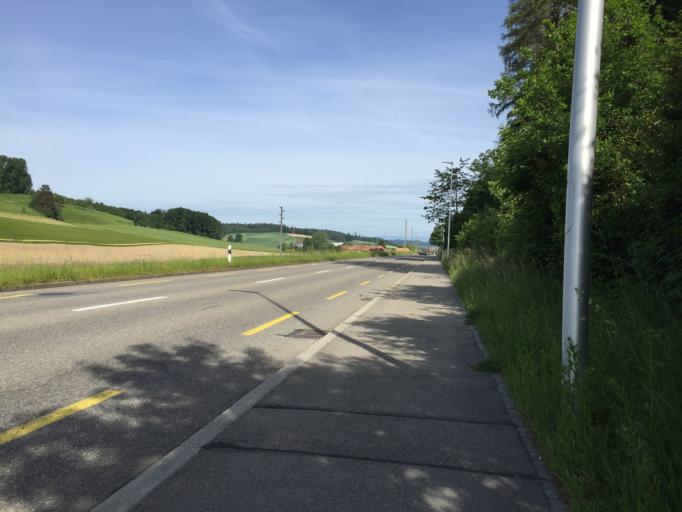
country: CH
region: Bern
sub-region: Bern-Mittelland District
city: Koniz
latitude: 46.9224
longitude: 7.3914
